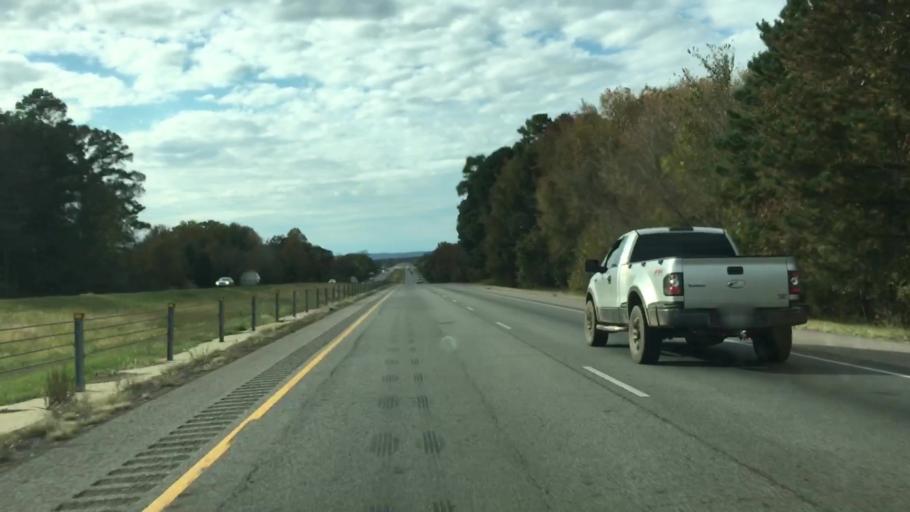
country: US
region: Arkansas
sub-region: Conway County
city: Morrilton
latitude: 35.1804
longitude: -92.7588
